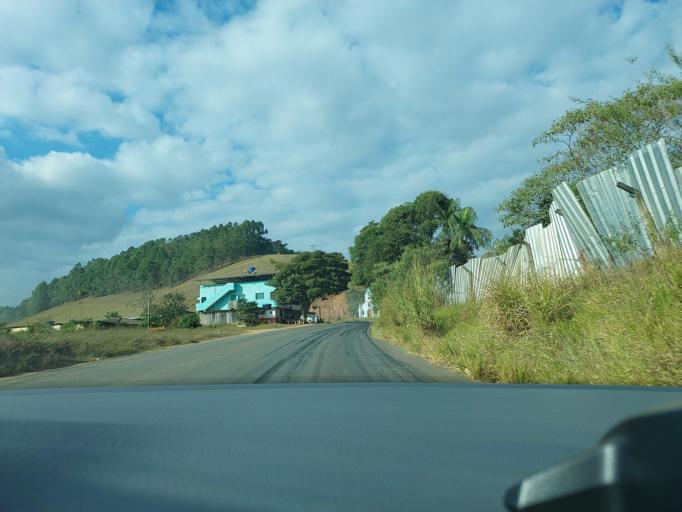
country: BR
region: Minas Gerais
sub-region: Vicosa
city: Vicosa
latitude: -20.8273
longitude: -42.7442
